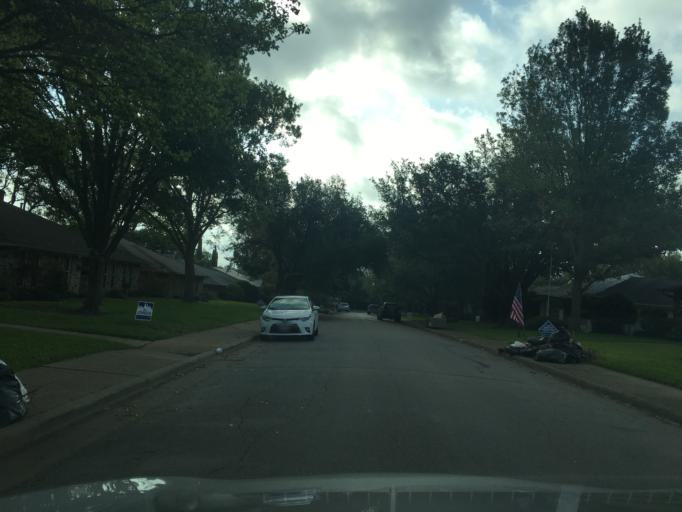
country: US
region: Texas
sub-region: Dallas County
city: Richardson
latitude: 32.8995
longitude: -96.7410
